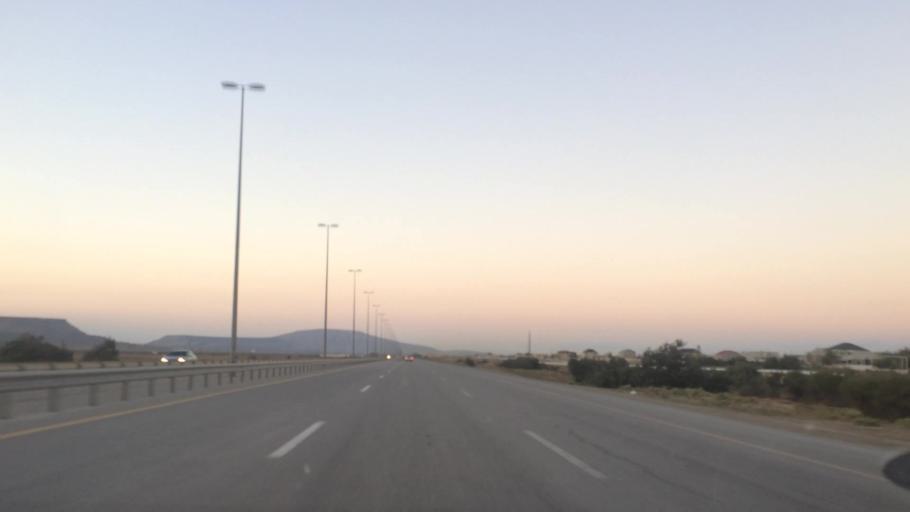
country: AZ
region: Baki
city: Qobustan
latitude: 40.0256
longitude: 49.4238
